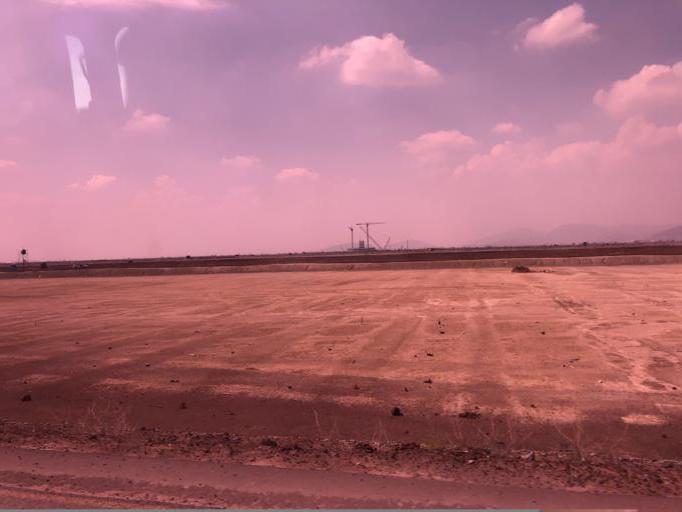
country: MX
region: Mexico
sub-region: Atenco
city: Colonia el Salado
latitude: 19.5245
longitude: -98.9857
